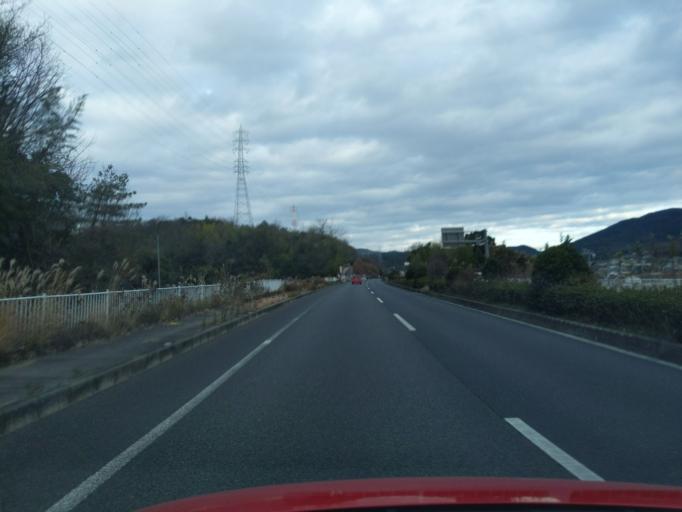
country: JP
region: Aichi
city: Kasugai
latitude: 35.3109
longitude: 137.0300
